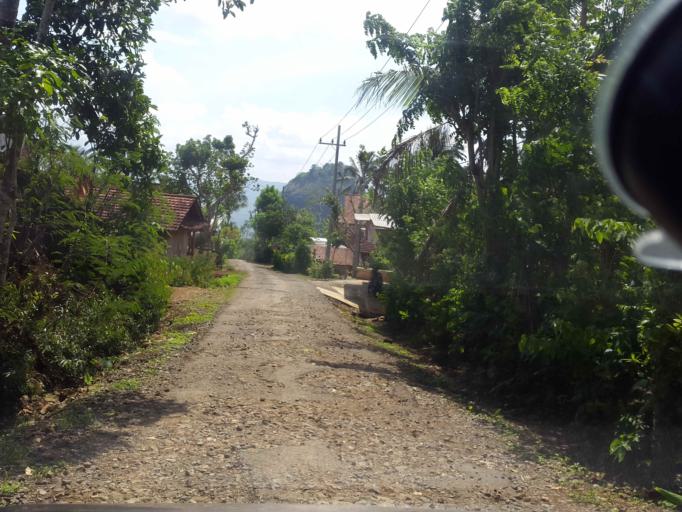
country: ID
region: East Java
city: Sidem
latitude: -8.1052
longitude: 111.5890
